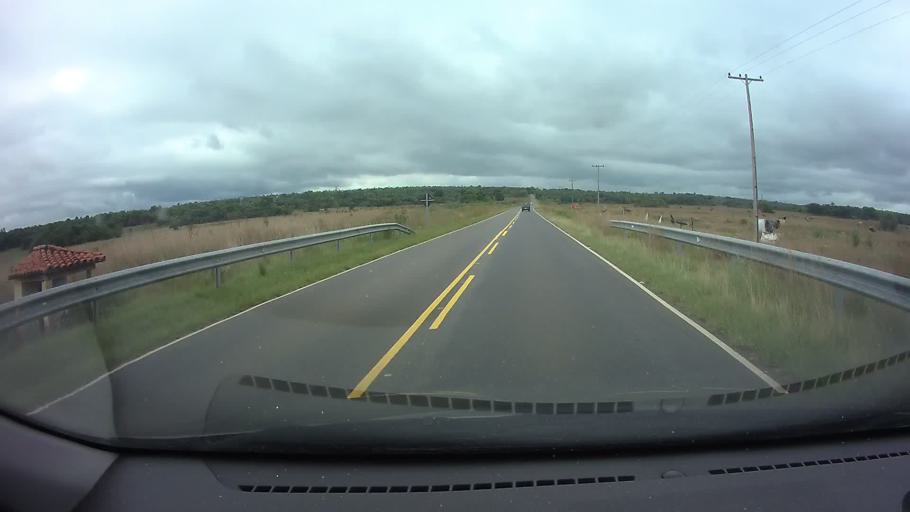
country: PY
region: Paraguari
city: Yaguaron
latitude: -25.7128
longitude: -57.3401
